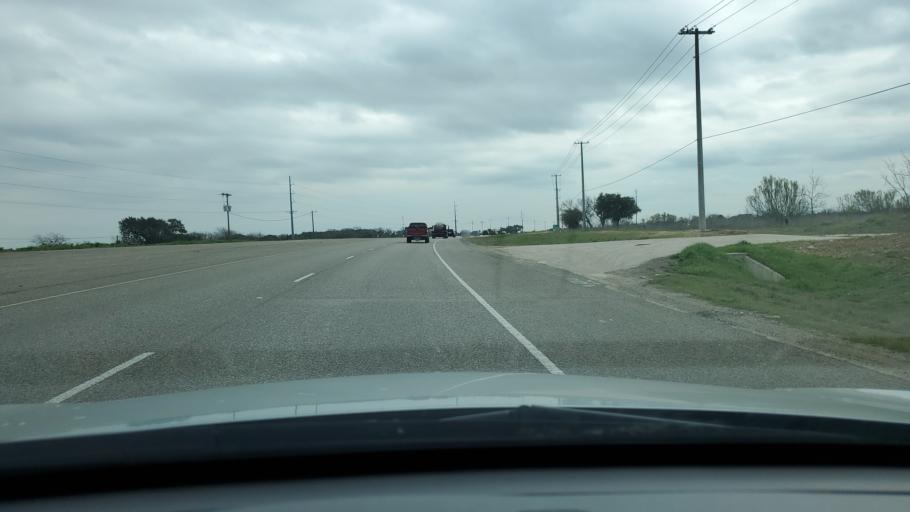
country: US
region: Texas
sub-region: Williamson County
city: Serenada
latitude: 30.7220
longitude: -97.6685
